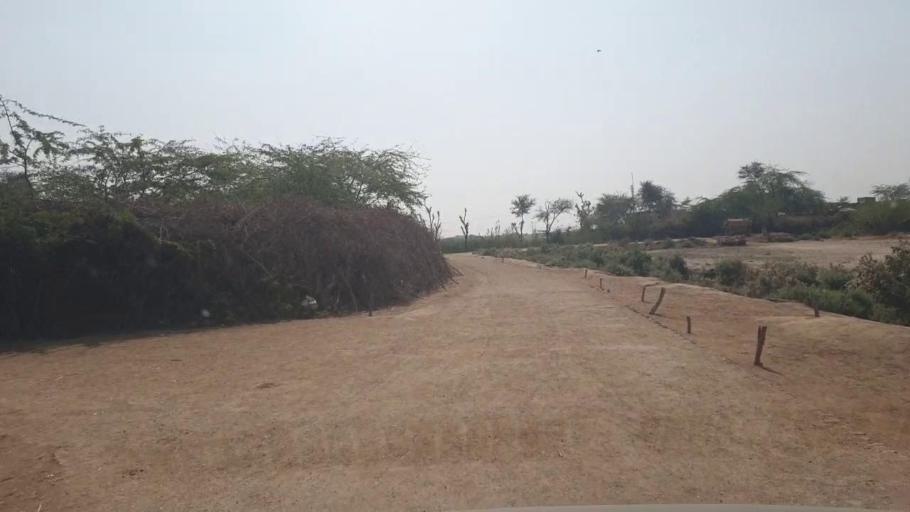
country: PK
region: Sindh
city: Dhoro Naro
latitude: 25.4654
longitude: 69.6128
